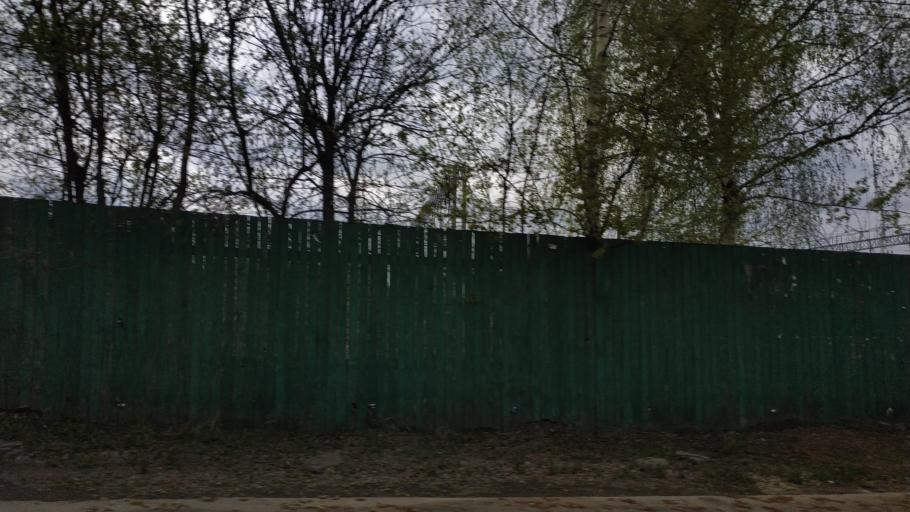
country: RU
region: Moskovskaya
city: Pavlovskiy Posad
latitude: 55.7761
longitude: 38.6827
